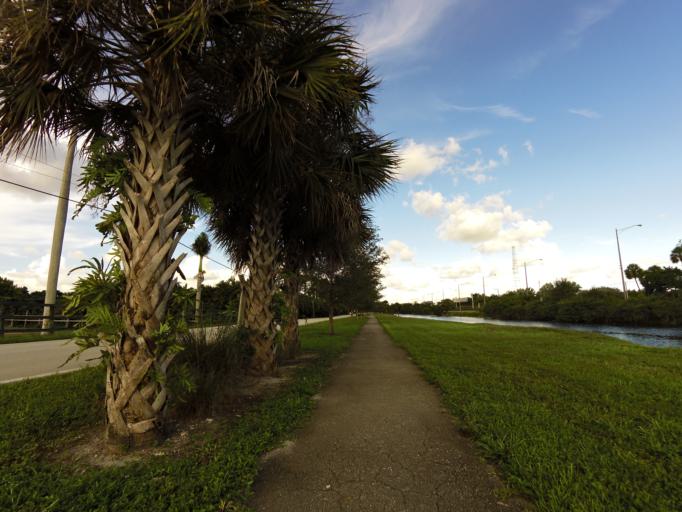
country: US
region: Florida
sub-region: Broward County
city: Cooper City
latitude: 26.0643
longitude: -80.3011
